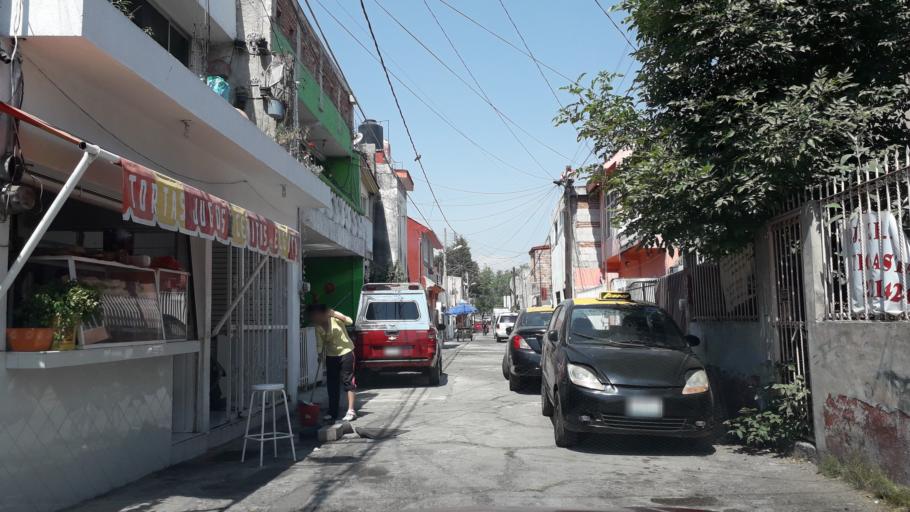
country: MX
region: Puebla
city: Puebla
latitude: 19.0781
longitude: -98.2155
